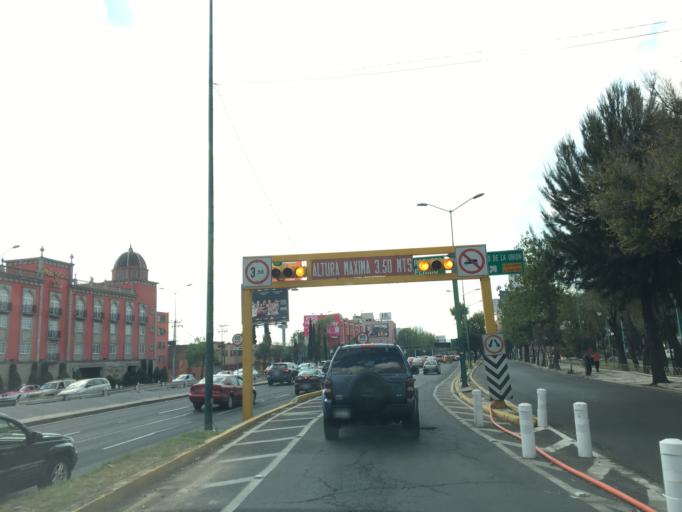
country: MX
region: Mexico City
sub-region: Iztacalco
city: Iztacalco
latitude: 19.4058
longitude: -99.1148
